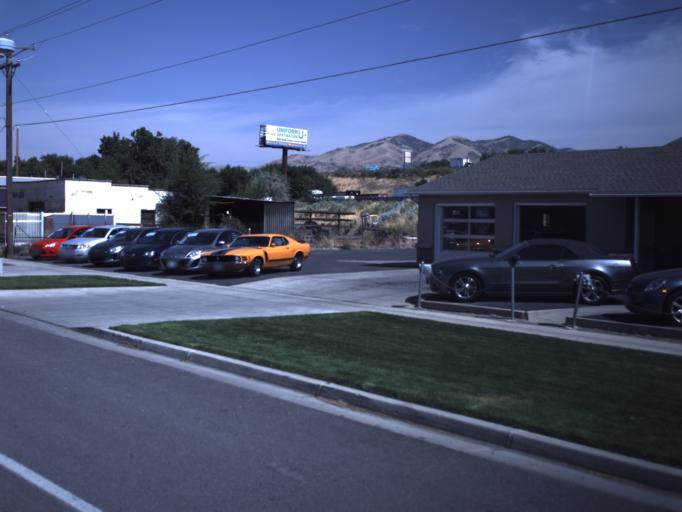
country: US
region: Utah
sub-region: Utah County
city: Lehi
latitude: 40.4042
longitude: -111.8576
